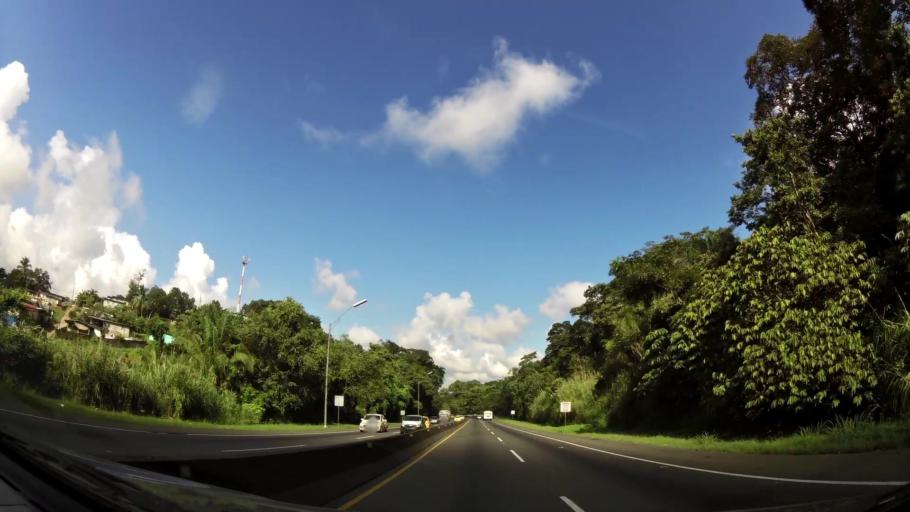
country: PA
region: Panama
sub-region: Distrito Arraijan
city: Arraijan
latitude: 8.9521
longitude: -79.6351
